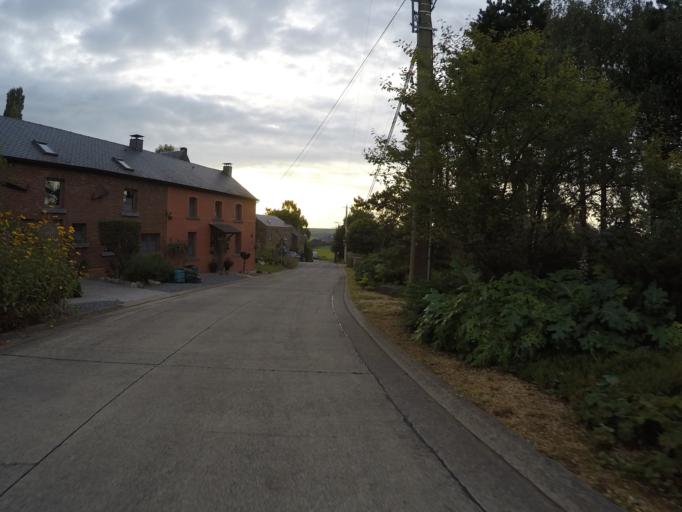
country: BE
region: Wallonia
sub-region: Province de Namur
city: Assesse
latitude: 50.3376
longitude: 5.0551
